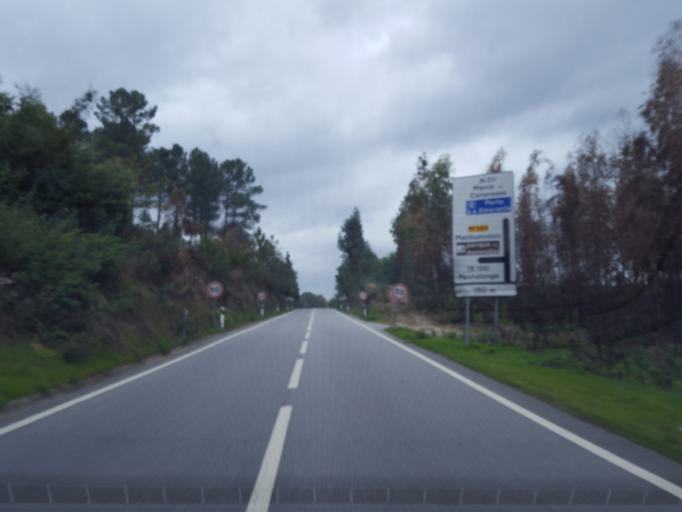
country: PT
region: Porto
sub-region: Marco de Canaveses
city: Marco de Canavezes
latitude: 41.1567
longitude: -8.1438
